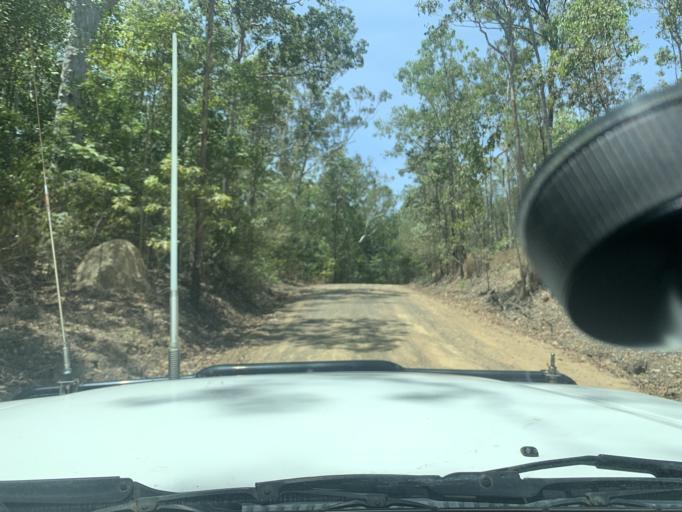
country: AU
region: Queensland
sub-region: Cairns
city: Redlynch
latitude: -16.9232
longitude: 145.6033
